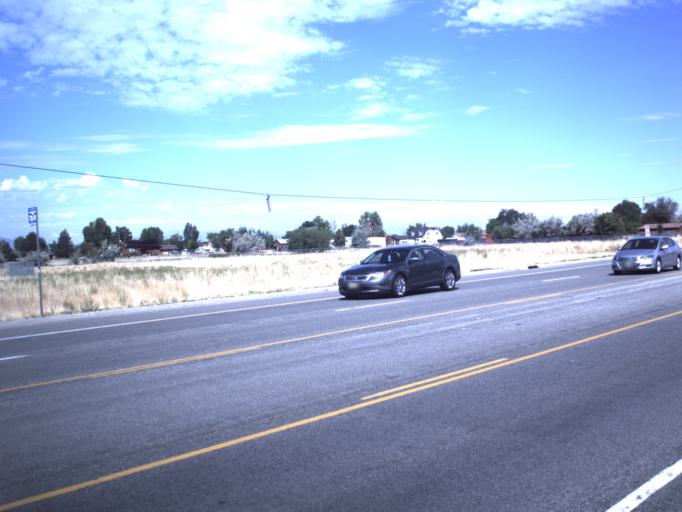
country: US
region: Utah
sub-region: Weber County
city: Harrisville
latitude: 41.2905
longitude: -111.9918
